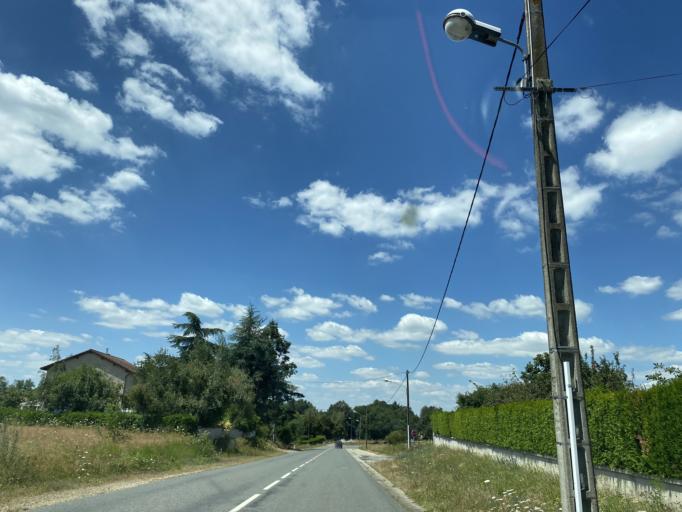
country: FR
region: Auvergne
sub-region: Departement du Puy-de-Dome
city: Peschadoires
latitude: 45.8674
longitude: 3.4921
